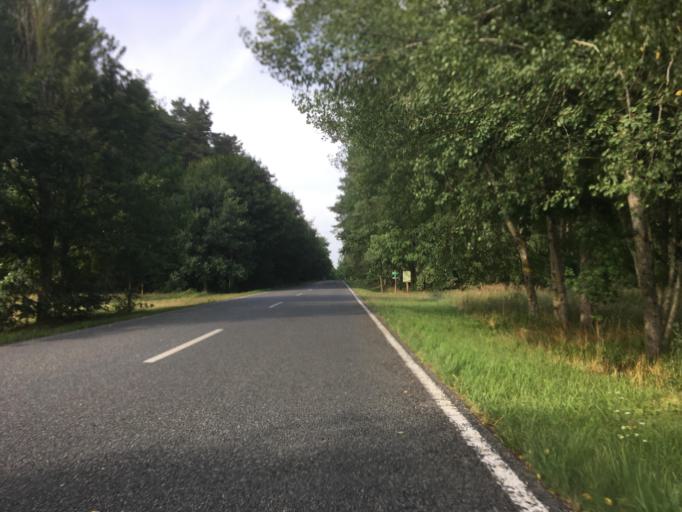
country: DE
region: Brandenburg
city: Biesenthal
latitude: 52.7746
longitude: 13.6528
